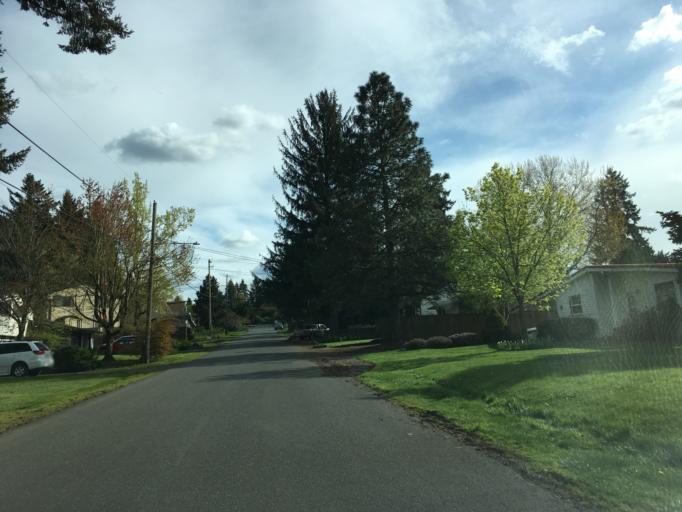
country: US
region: Oregon
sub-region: Multnomah County
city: Lents
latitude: 45.5509
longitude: -122.5506
